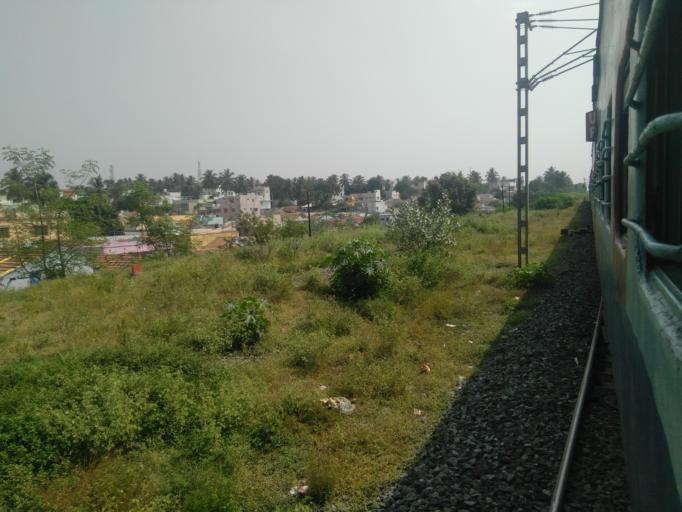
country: IN
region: Tamil Nadu
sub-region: Coimbatore
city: Mettupalayam
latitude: 11.2927
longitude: 76.9370
